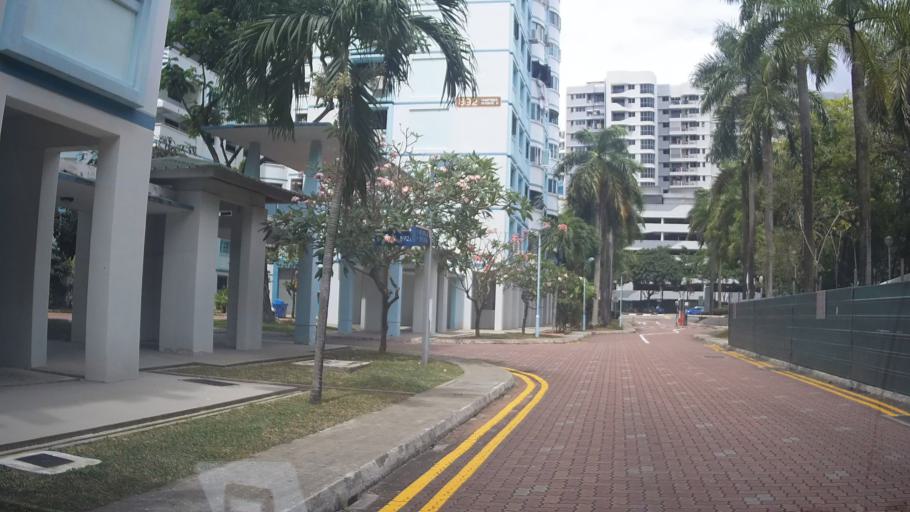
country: SG
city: Singapore
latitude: 1.3492
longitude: 103.9299
